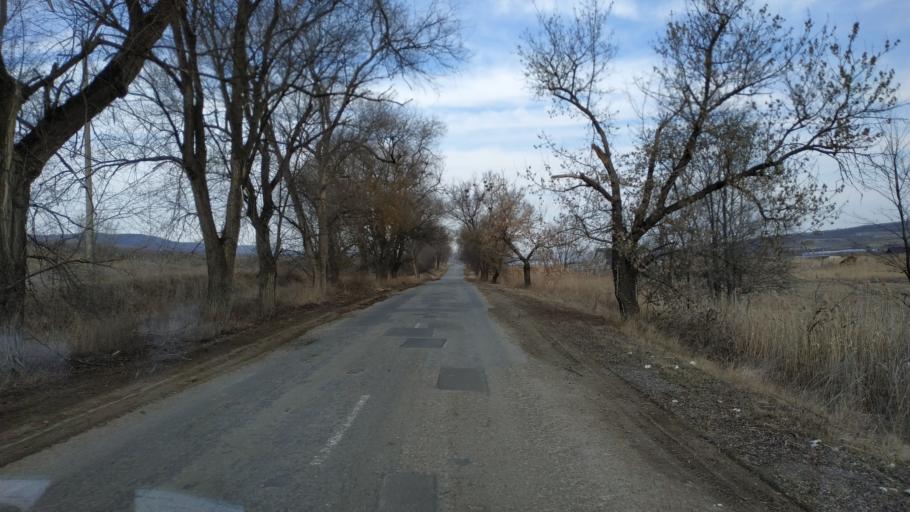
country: MD
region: Nisporeni
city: Nisporeni
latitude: 47.0896
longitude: 28.1376
